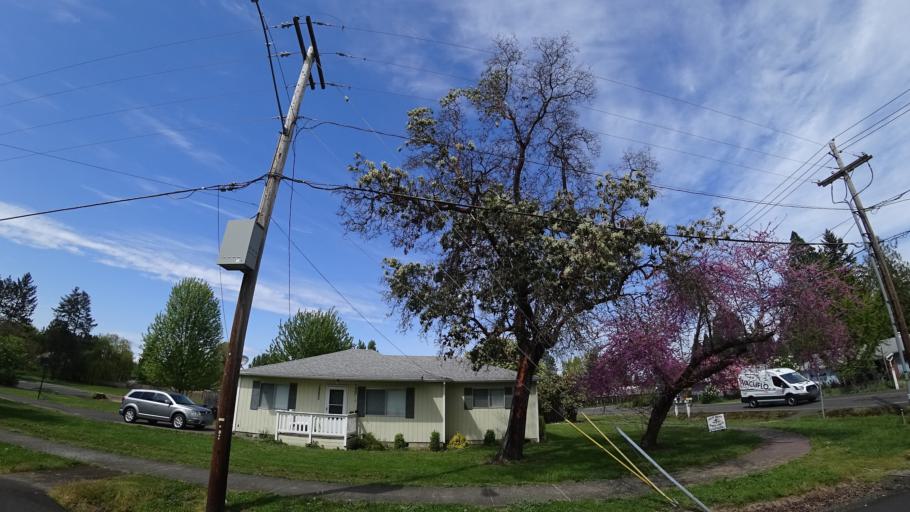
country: US
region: Oregon
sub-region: Washington County
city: Aloha
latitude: 45.4890
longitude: -122.8818
